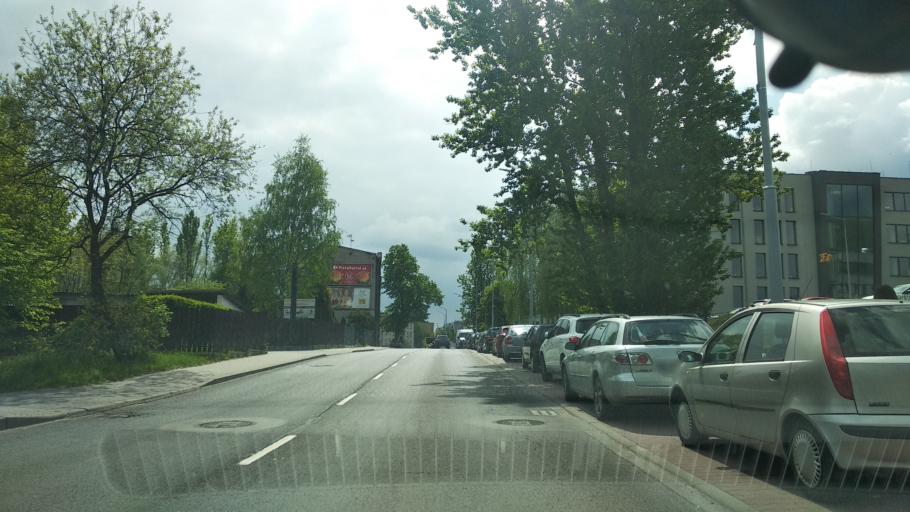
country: PL
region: Silesian Voivodeship
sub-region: Katowice
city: Katowice
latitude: 50.2373
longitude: 18.9790
